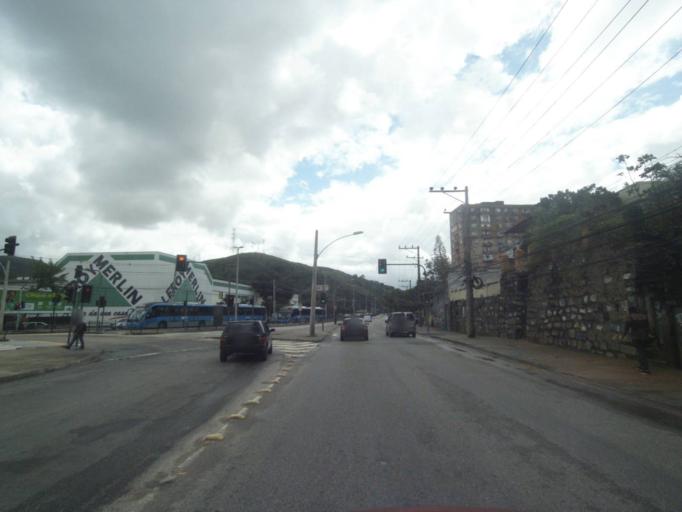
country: BR
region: Rio de Janeiro
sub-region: Sao Joao De Meriti
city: Sao Joao de Meriti
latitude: -22.9150
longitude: -43.3607
